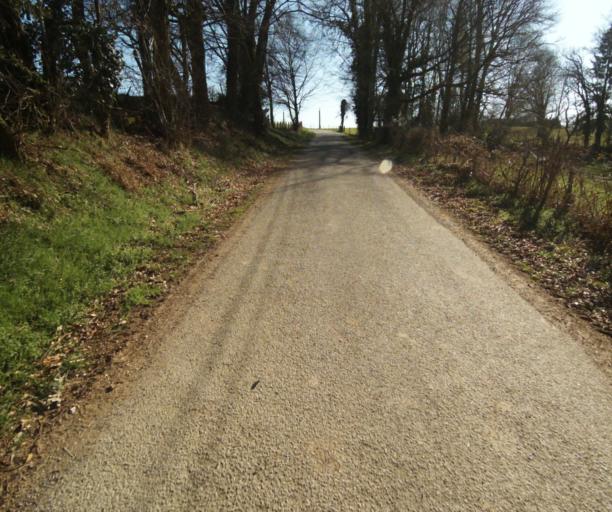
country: FR
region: Limousin
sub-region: Departement de la Correze
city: Chamboulive
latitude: 45.4728
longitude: 1.7000
